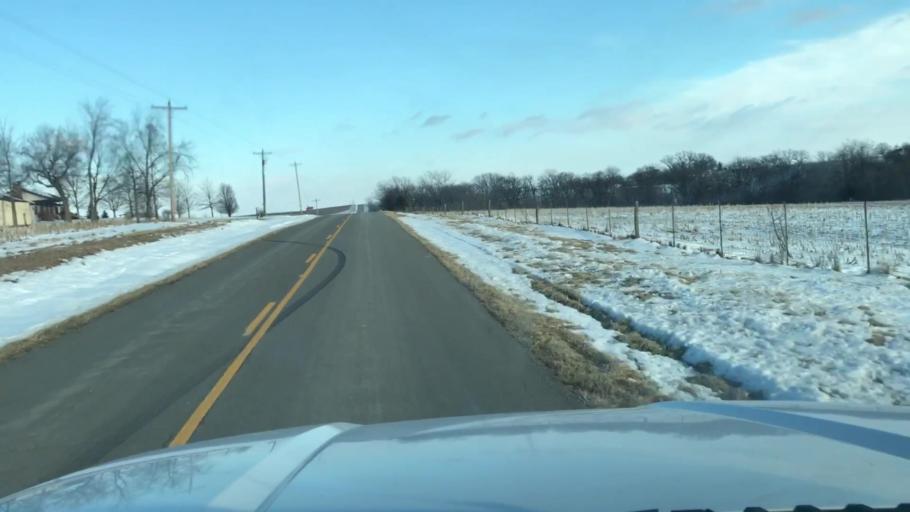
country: US
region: Missouri
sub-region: Holt County
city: Oregon
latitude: 40.1007
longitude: -95.0080
